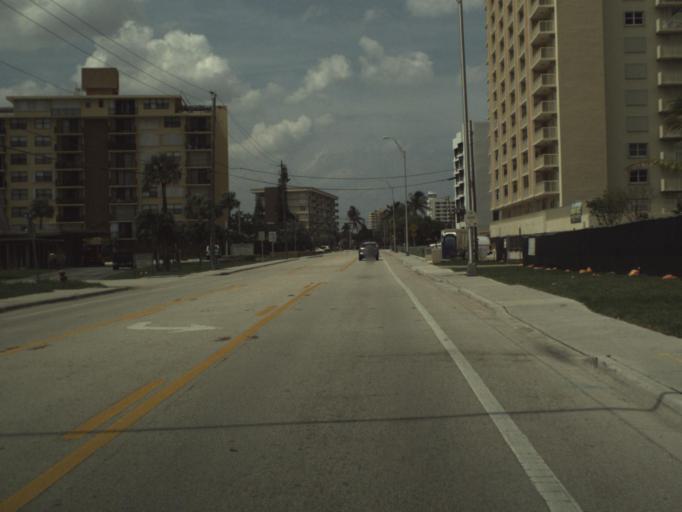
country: US
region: Florida
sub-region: Broward County
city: Terra Mar
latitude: 26.2436
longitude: -80.0877
